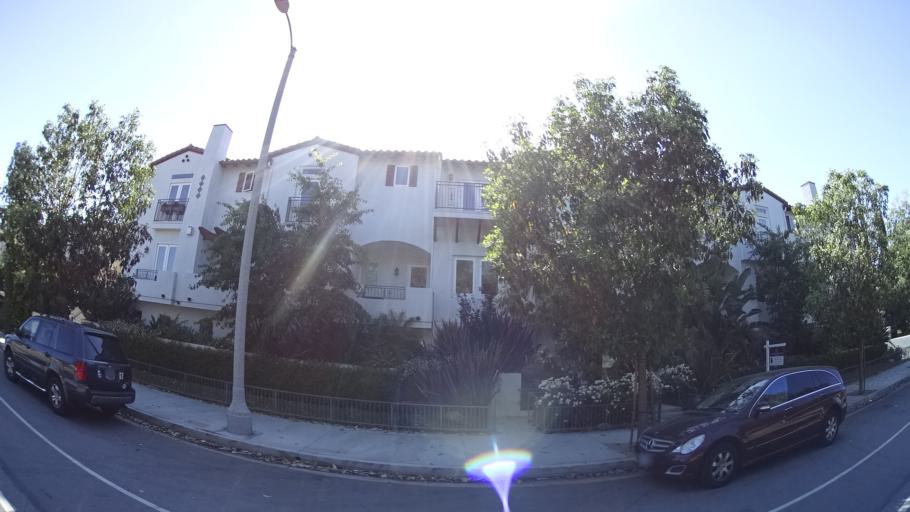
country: US
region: California
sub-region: Los Angeles County
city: North Hollywood
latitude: 34.1535
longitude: -118.3878
